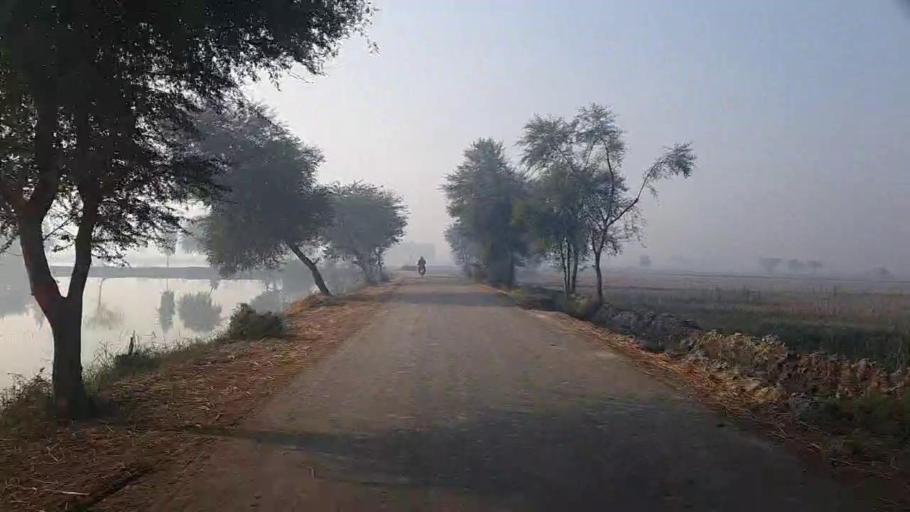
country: PK
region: Sindh
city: Mehar
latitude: 27.1486
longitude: 67.8232
